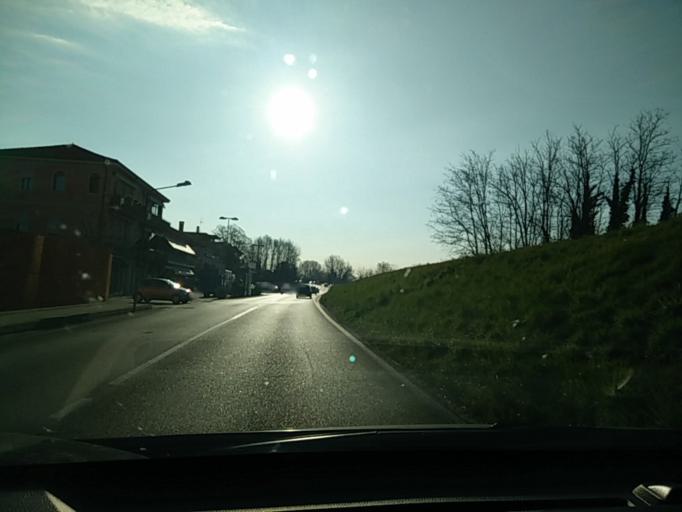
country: IT
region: Veneto
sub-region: Provincia di Venezia
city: Eraclea
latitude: 45.5753
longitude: 12.6711
